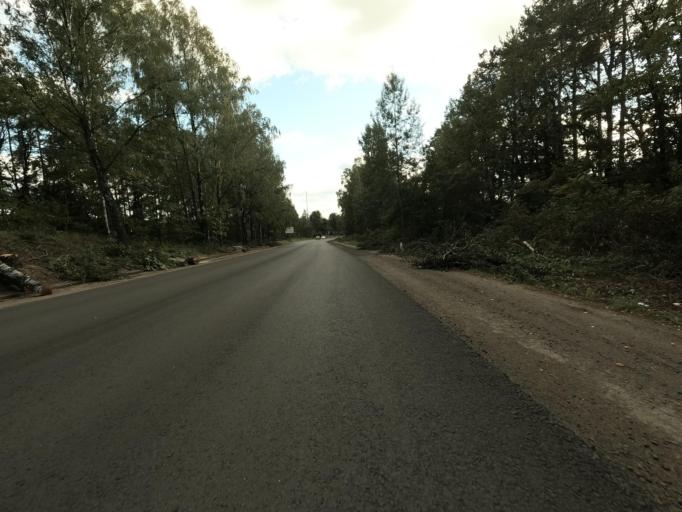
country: RU
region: Leningrad
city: Koltushi
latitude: 59.9491
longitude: 30.6572
